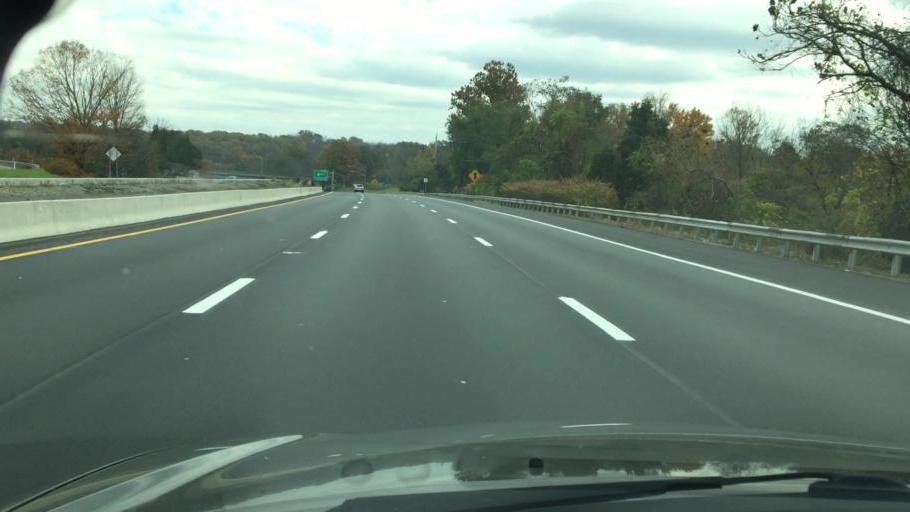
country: US
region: New Jersey
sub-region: Warren County
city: Belvidere
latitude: 40.9285
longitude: -75.0934
